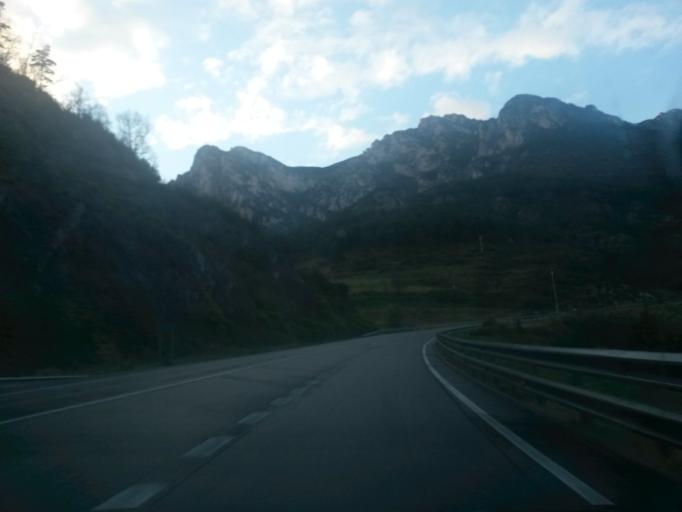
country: ES
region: Catalonia
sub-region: Provincia de Barcelona
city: Baga
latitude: 42.2835
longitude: 1.8504
